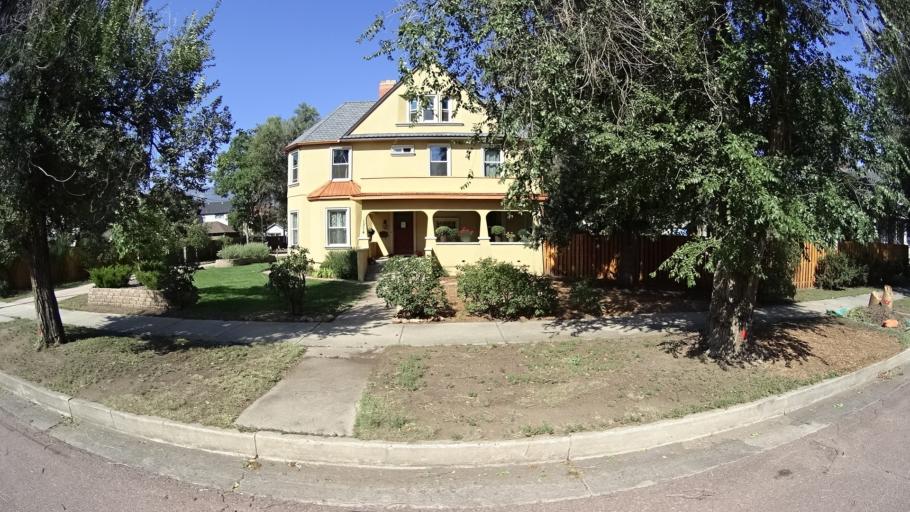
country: US
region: Colorado
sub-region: El Paso County
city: Colorado Springs
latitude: 38.8525
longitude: -104.8189
